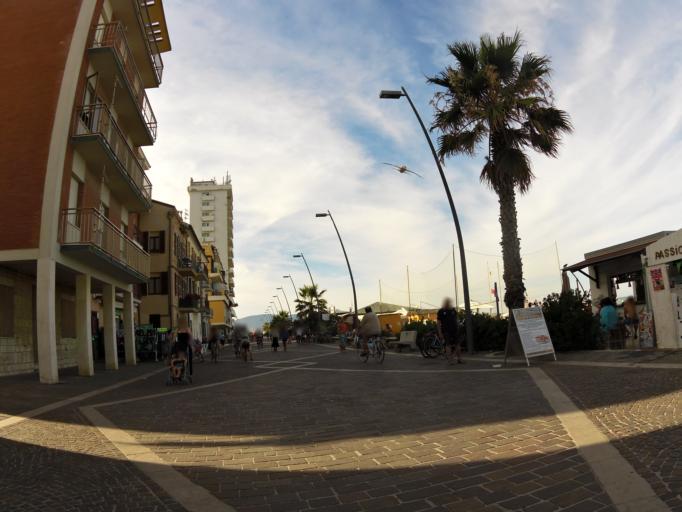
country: IT
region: The Marches
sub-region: Provincia di Macerata
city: Porto Recanati
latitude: 43.4342
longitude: 13.6647
